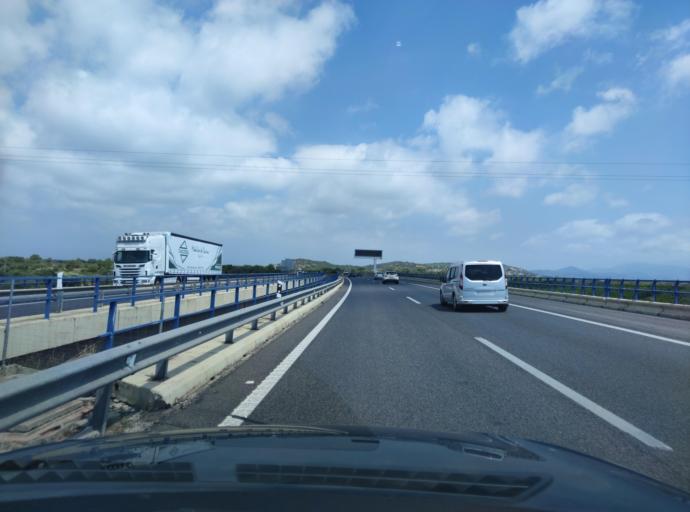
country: ES
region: Valencia
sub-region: Provincia de Castello
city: Vinaros
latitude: 40.4756
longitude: 0.4189
